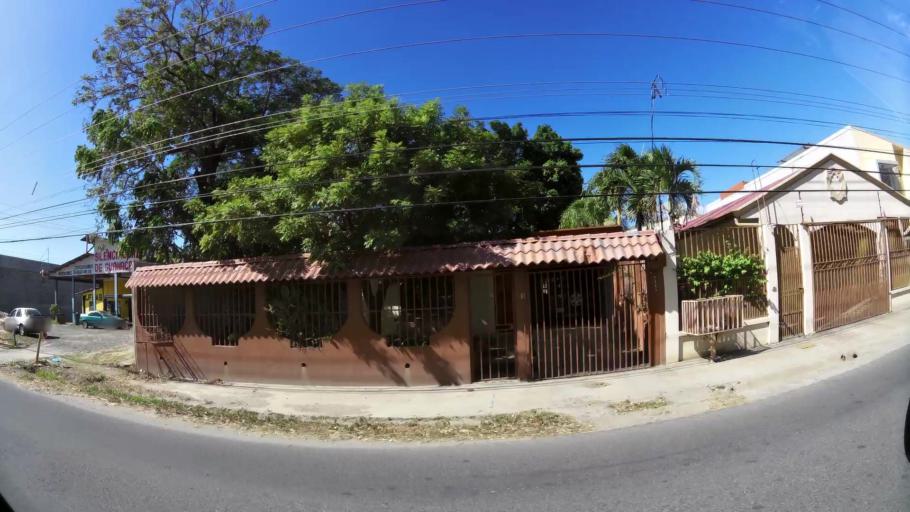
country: CR
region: Guanacaste
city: Liberia
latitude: 10.6313
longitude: -85.4460
